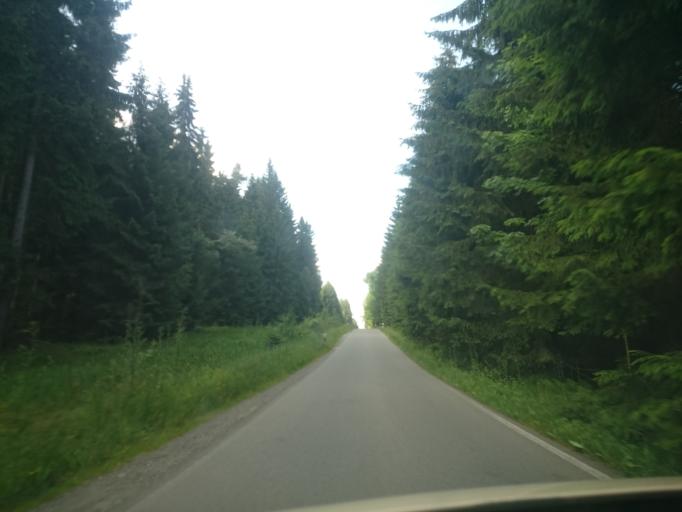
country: DE
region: Saxony
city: Eppendorf
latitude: 50.7684
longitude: 13.2254
